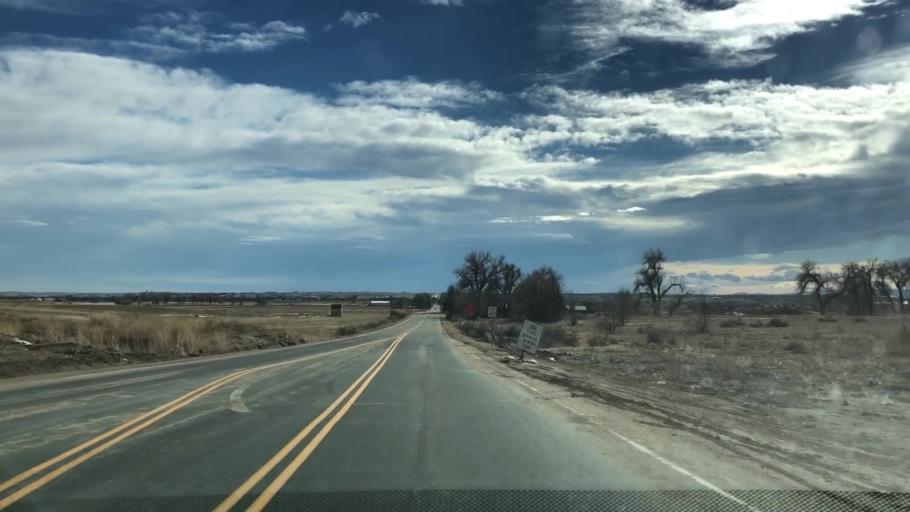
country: US
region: Colorado
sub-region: Weld County
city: Windsor
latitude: 40.5224
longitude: -104.9443
